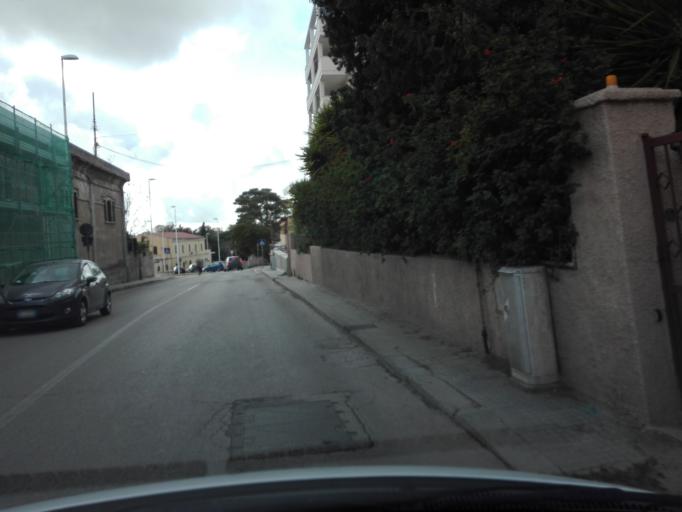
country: IT
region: Sardinia
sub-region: Provincia di Sassari
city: Sassari
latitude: 40.7163
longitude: 8.5771
